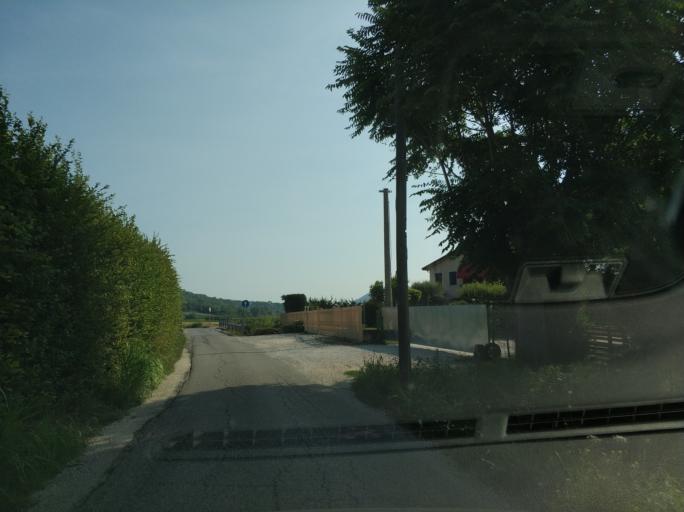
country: IT
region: Veneto
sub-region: Provincia di Padova
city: Baone
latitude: 45.2296
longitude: 11.6912
